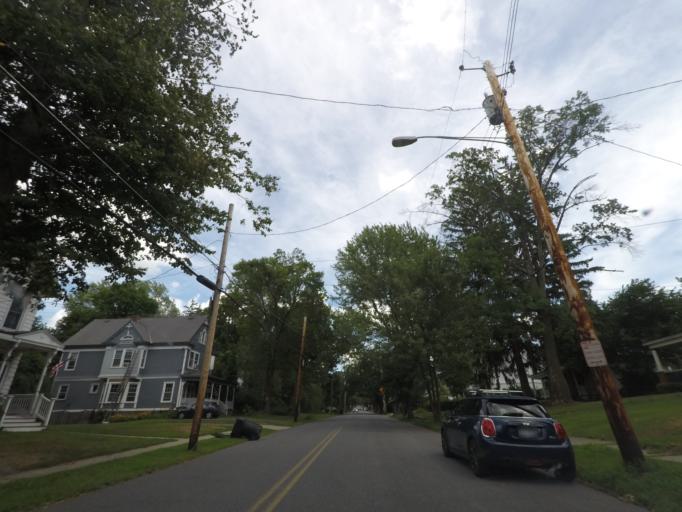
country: US
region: New York
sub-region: Rensselaer County
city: Troy
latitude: 42.7178
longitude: -73.6697
